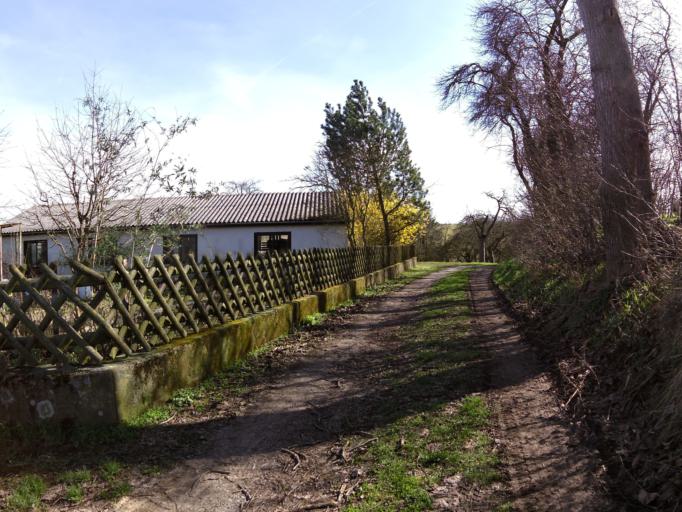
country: DE
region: Bavaria
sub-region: Regierungsbezirk Unterfranken
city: Buchbrunn
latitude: 49.7476
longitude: 10.1239
